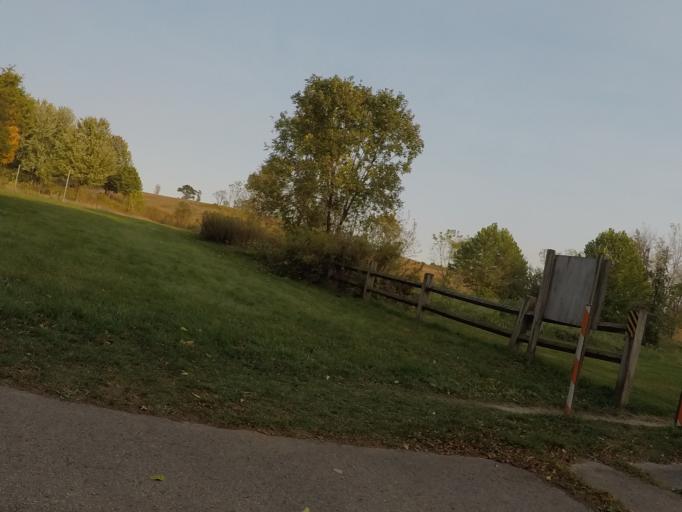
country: US
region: Wisconsin
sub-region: Dane County
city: Verona
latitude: 42.9993
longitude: -89.5284
